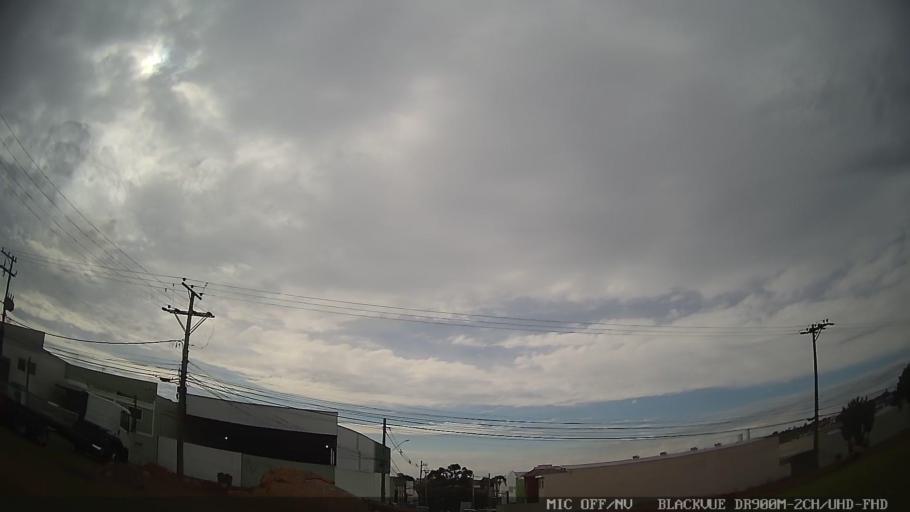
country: BR
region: Sao Paulo
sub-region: Salto
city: Salto
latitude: -23.2158
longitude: -47.2673
